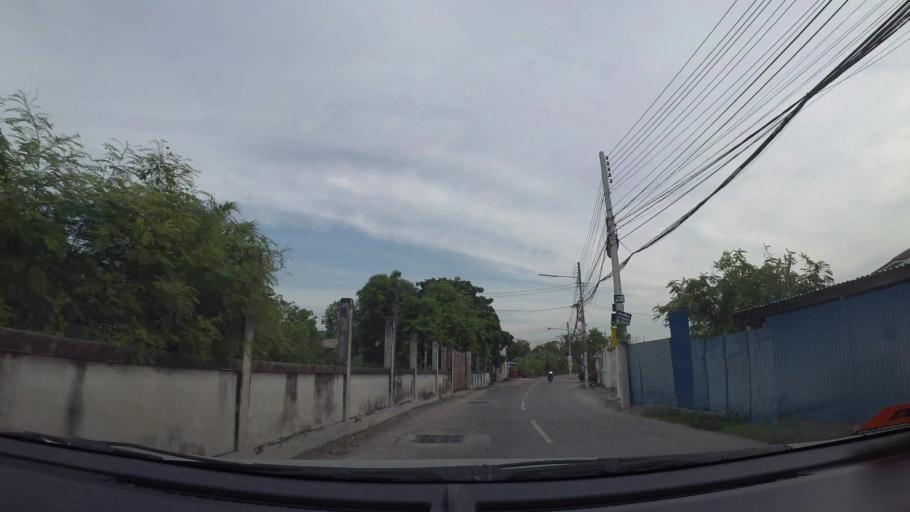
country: TH
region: Chon Buri
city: Chon Buri
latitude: 13.3385
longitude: 100.9807
